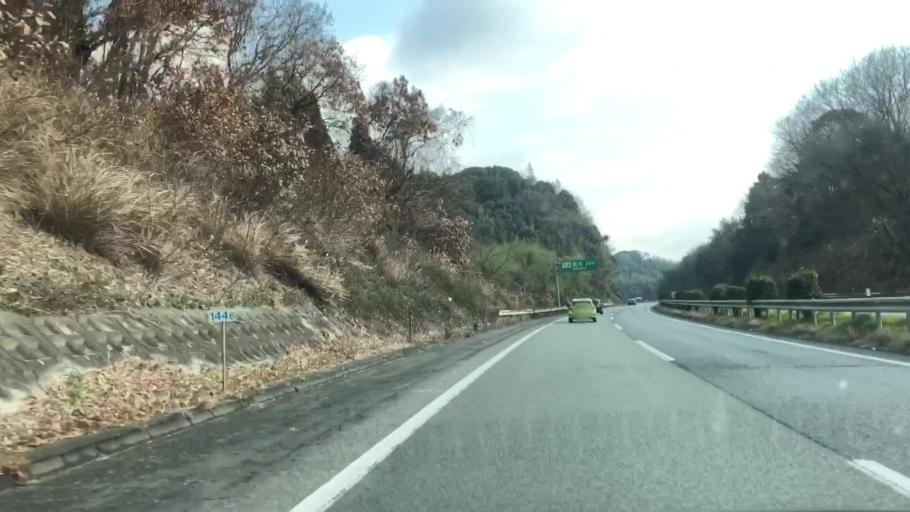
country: JP
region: Kumamoto
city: Tamana
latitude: 33.0007
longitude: 130.5898
